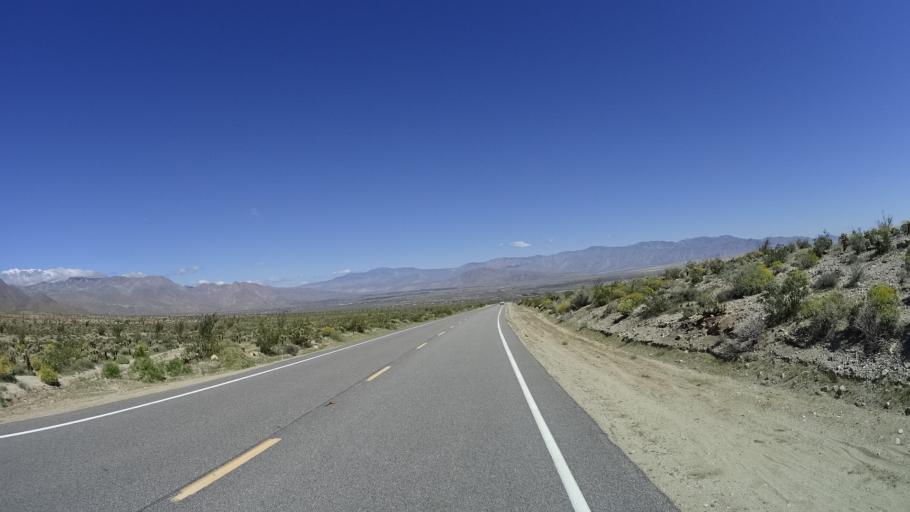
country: US
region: California
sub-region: San Diego County
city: Borrego Springs
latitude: 33.1677
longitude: -116.3357
